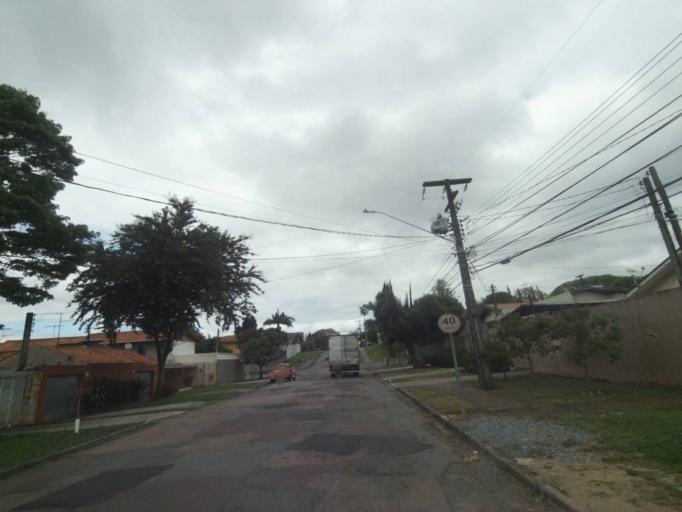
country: BR
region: Parana
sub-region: Pinhais
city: Pinhais
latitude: -25.4059
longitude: -49.2242
